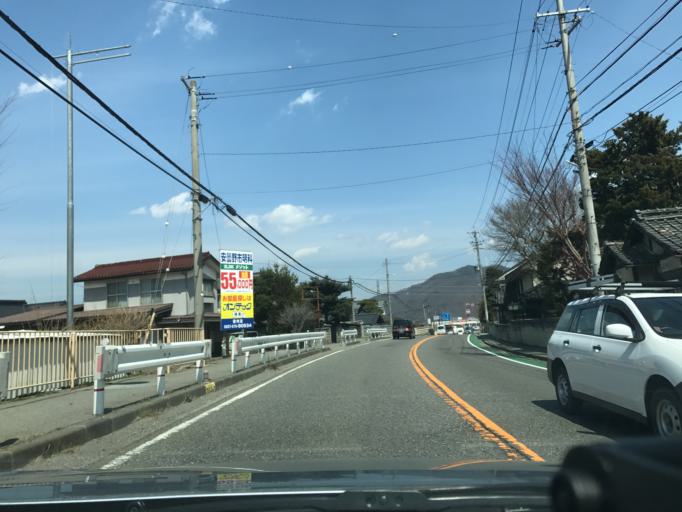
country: JP
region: Nagano
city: Hotaka
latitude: 36.3466
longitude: 137.9220
